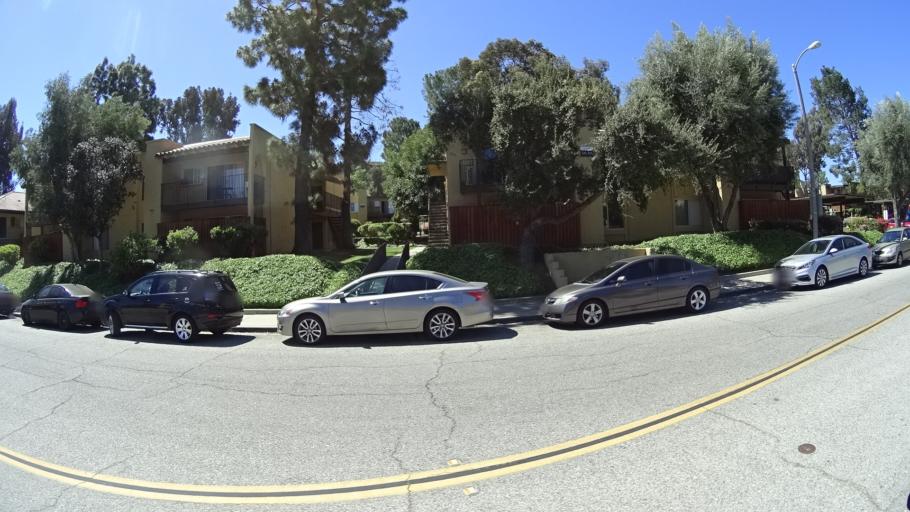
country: US
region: California
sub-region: Ventura County
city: Thousand Oaks
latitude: 34.1743
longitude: -118.8707
